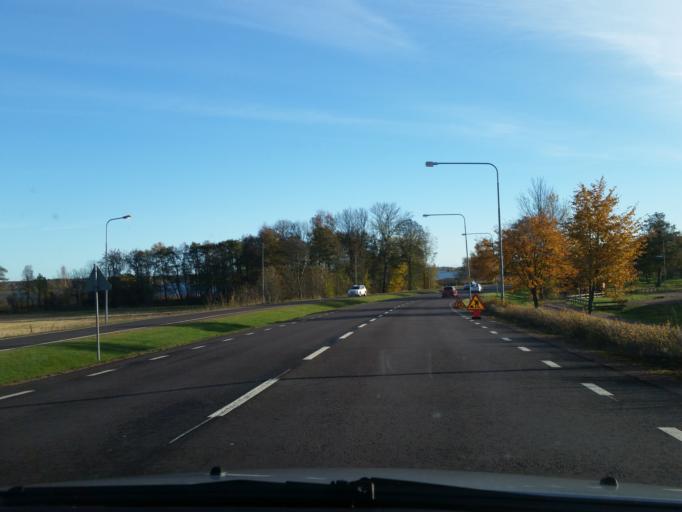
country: AX
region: Mariehamns stad
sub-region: Mariehamn
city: Mariehamn
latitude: 60.1131
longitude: 19.9413
